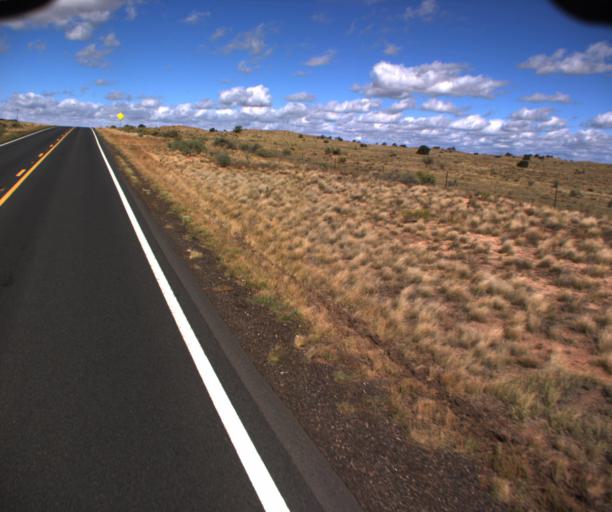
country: US
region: Arizona
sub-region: Apache County
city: Houck
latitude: 35.0319
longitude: -109.2564
